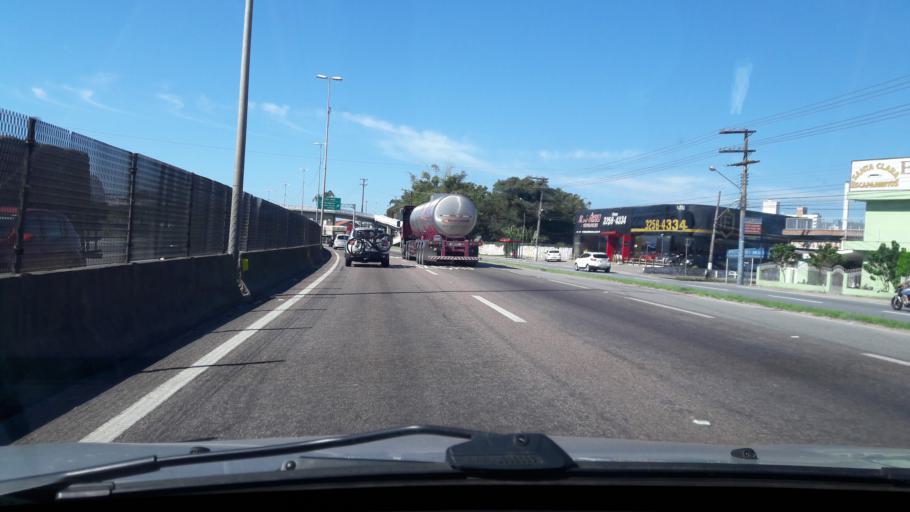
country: BR
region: Santa Catarina
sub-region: Sao Jose
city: Campinas
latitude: -27.5555
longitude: -48.6193
